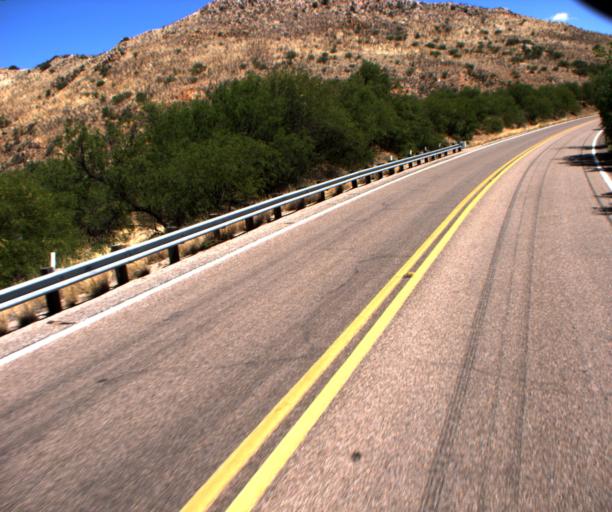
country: US
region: Arizona
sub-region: Santa Cruz County
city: Rio Rico
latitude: 31.5044
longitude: -110.8084
